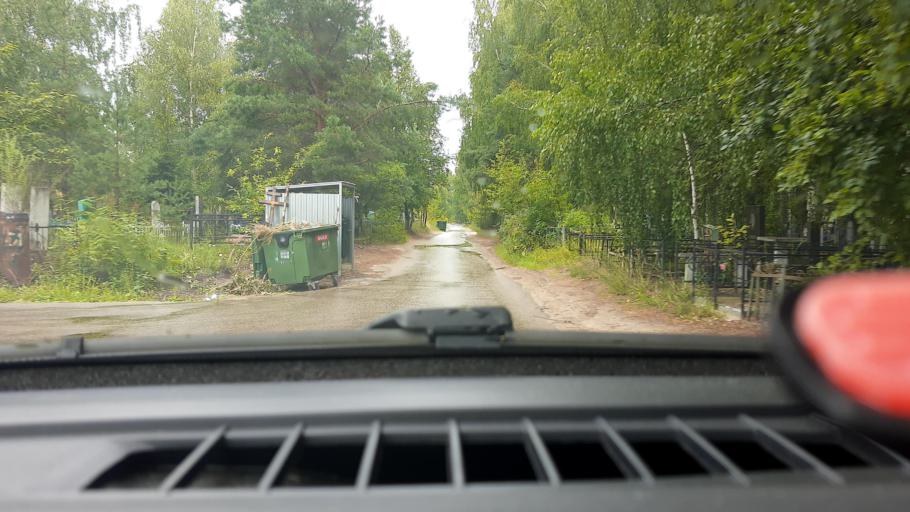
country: RU
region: Nizjnij Novgorod
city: Gorbatovka
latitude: 56.3544
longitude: 43.7776
